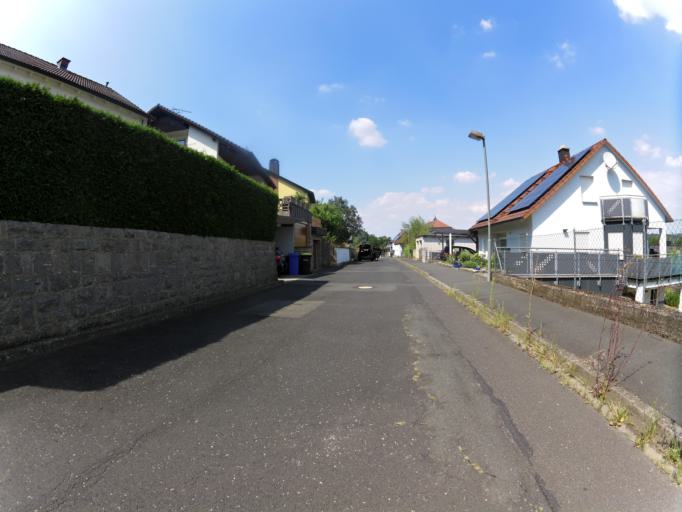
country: DE
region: Bavaria
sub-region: Regierungsbezirk Unterfranken
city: Ochsenfurt
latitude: 49.6591
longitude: 10.0584
